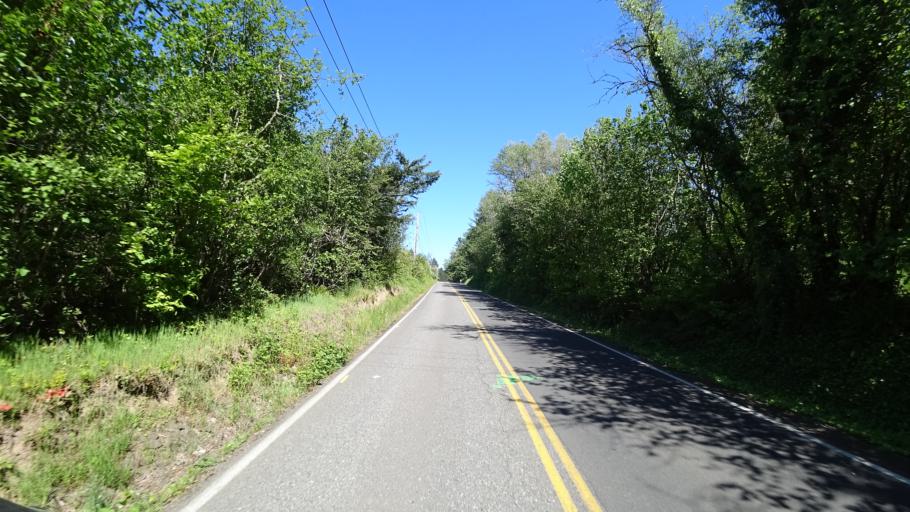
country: US
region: Oregon
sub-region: Washington County
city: Cedar Mill
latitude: 45.5542
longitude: -122.8017
